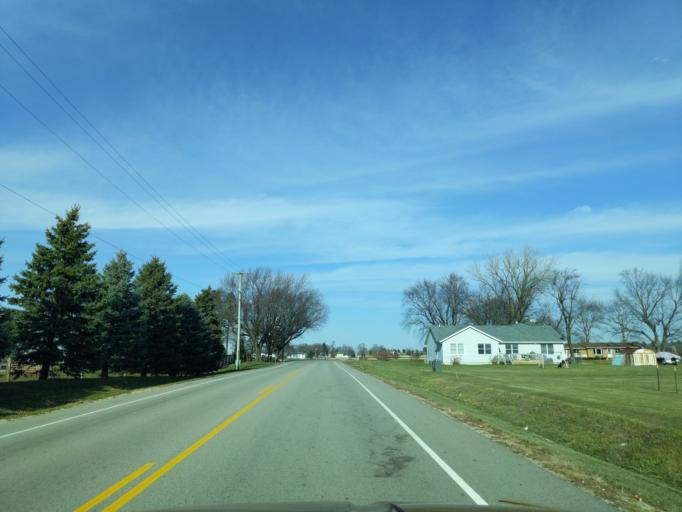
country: US
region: Wisconsin
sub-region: Walworth County
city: Elkhorn
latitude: 42.7264
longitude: -88.5820
